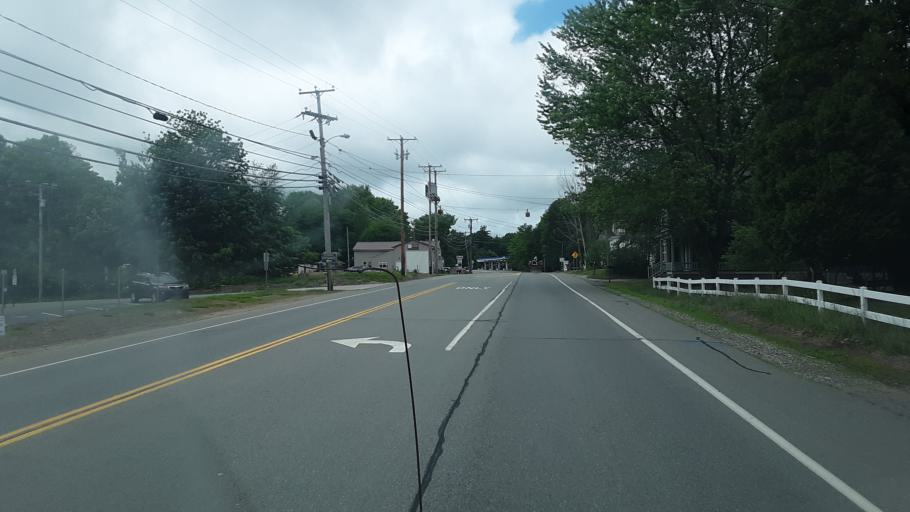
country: US
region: New Hampshire
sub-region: Rockingham County
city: Northwood
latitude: 43.2084
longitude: -71.1764
